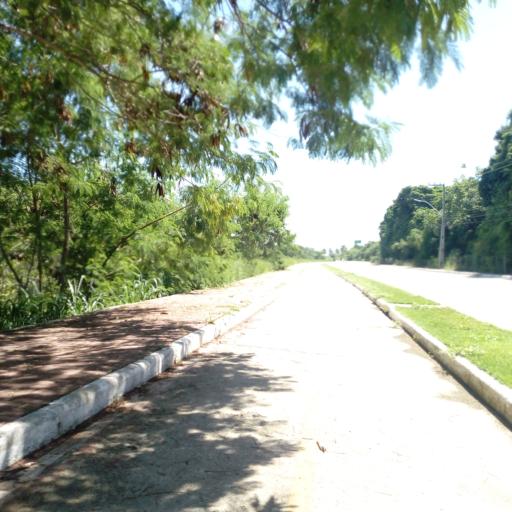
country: BR
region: Pernambuco
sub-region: Sirinhaem
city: Sirinhaem
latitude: -8.5236
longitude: -35.0106
